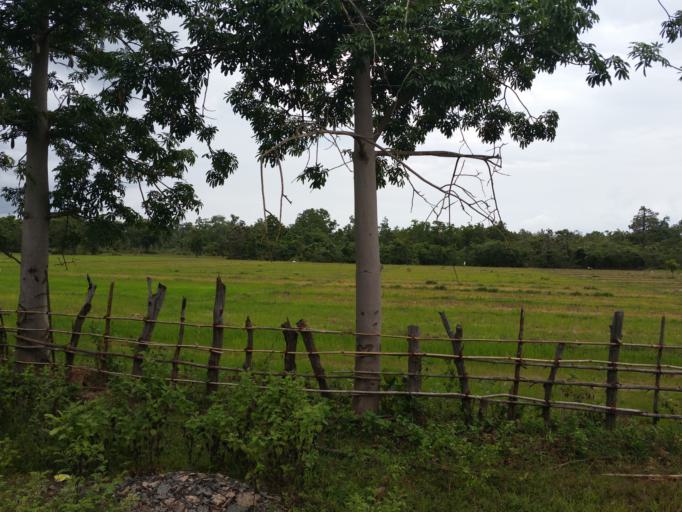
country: KH
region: Stung Treng
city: Stung Treng
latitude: 13.1706
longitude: 106.1359
